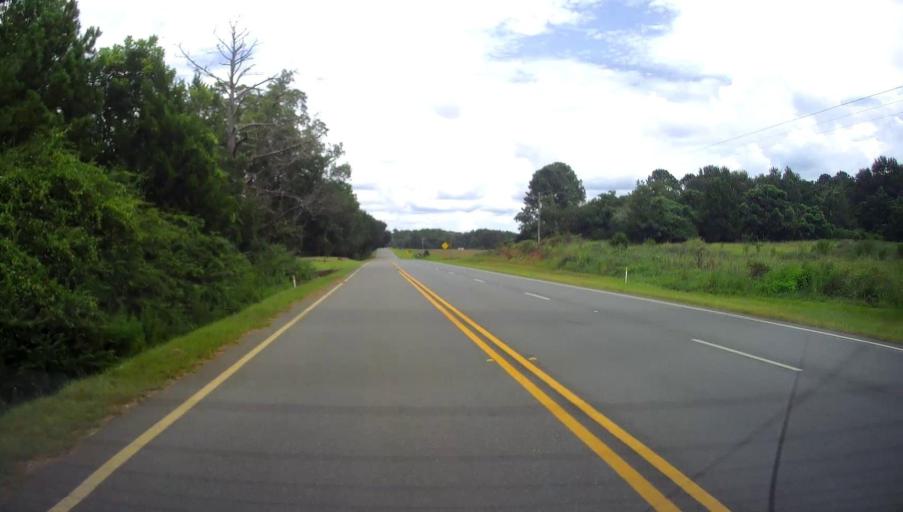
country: US
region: Georgia
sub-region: Schley County
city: Ellaville
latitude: 32.2579
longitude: -84.2361
